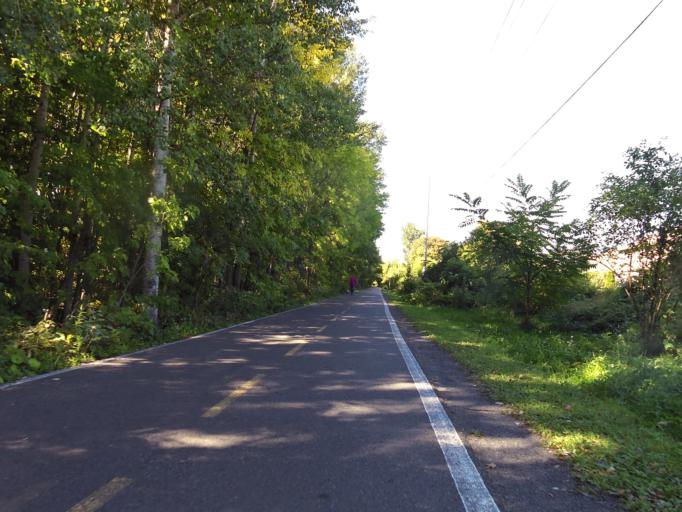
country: CA
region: Ontario
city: Bourget
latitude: 45.2637
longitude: -75.3562
